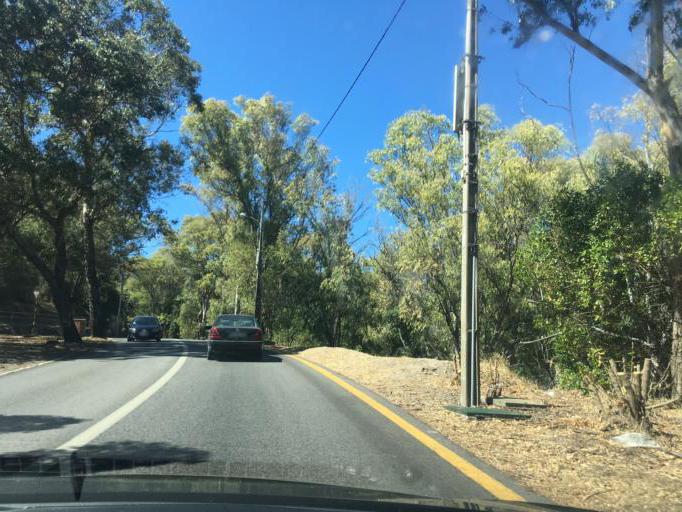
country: PT
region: Lisbon
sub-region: Odivelas
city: Pontinha
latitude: 38.7235
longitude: -9.1871
